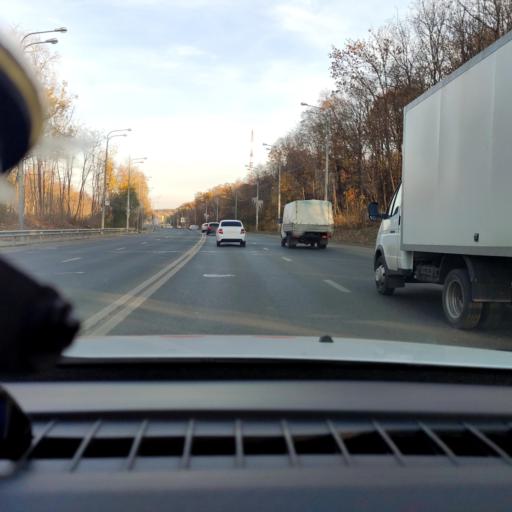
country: RU
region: Samara
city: Samara
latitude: 53.2818
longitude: 50.2287
